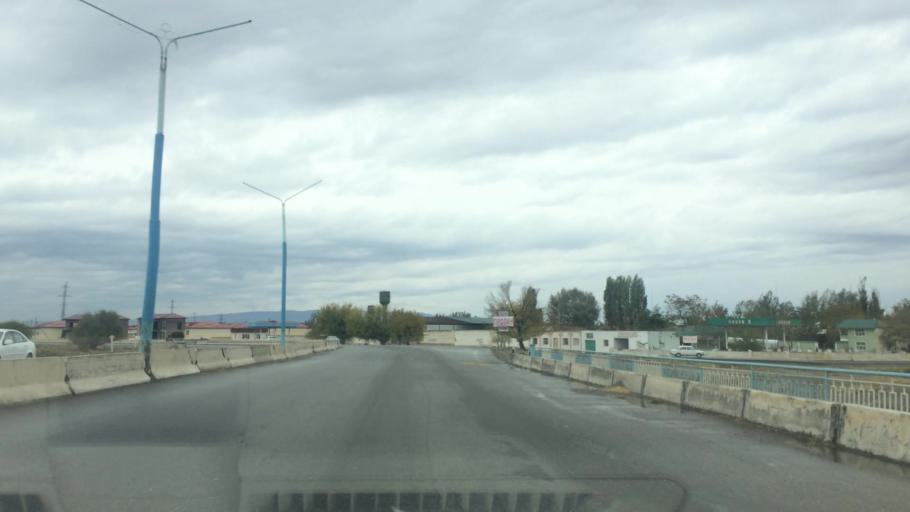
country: UZ
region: Jizzax
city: Jizzax
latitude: 40.0267
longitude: 67.6181
